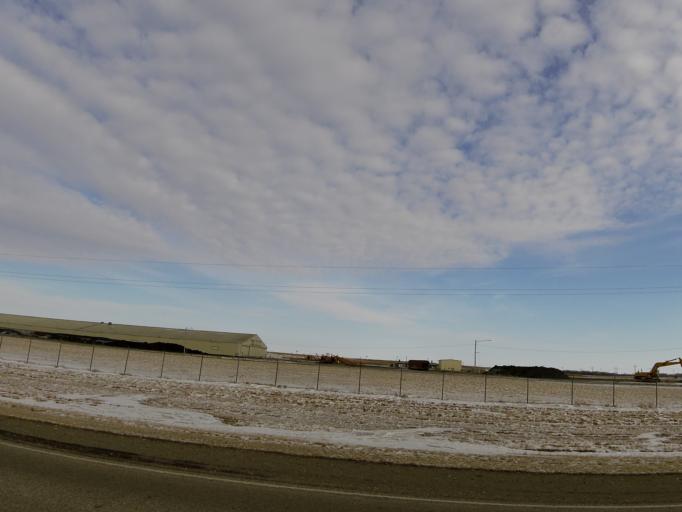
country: US
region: North Dakota
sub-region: Walsh County
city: Grafton
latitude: 48.5882
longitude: -97.1788
